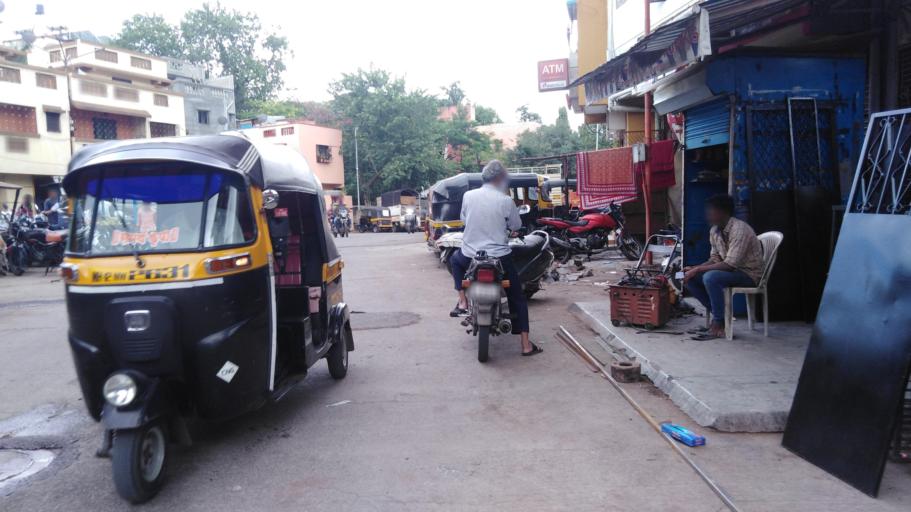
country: IN
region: Maharashtra
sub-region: Pune Division
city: Shivaji Nagar
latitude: 18.5469
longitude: 73.8783
